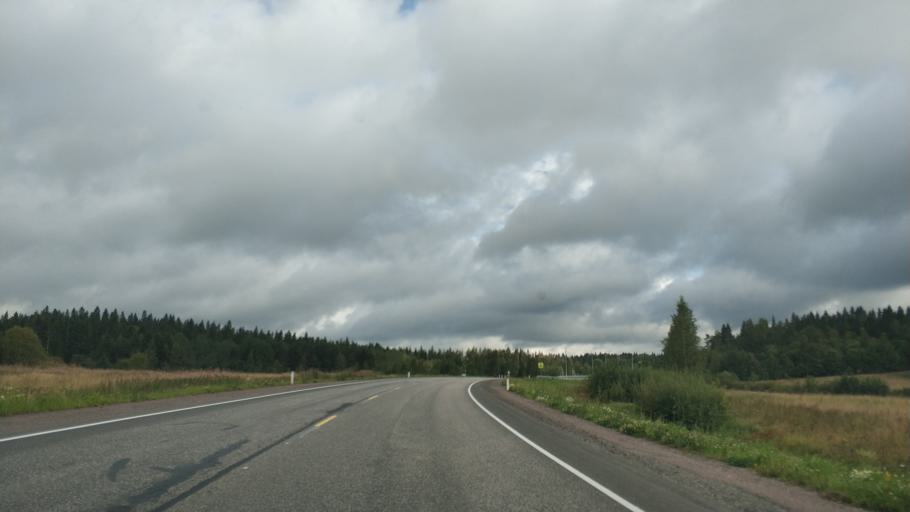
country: RU
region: Republic of Karelia
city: Khelyulya
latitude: 61.7987
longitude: 30.6156
